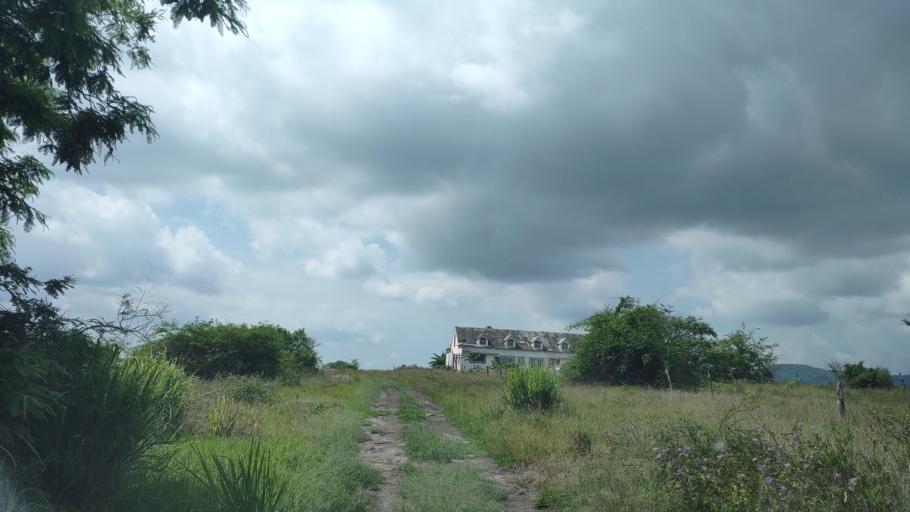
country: MX
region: Veracruz
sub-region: Emiliano Zapata
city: Dos Rios
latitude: 19.4623
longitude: -96.7967
